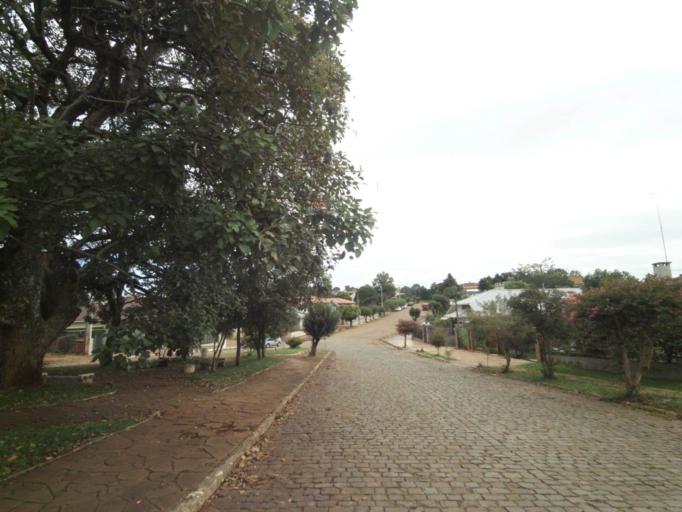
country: BR
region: Rio Grande do Sul
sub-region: Lagoa Vermelha
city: Lagoa Vermelha
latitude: -28.2090
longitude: -51.5171
